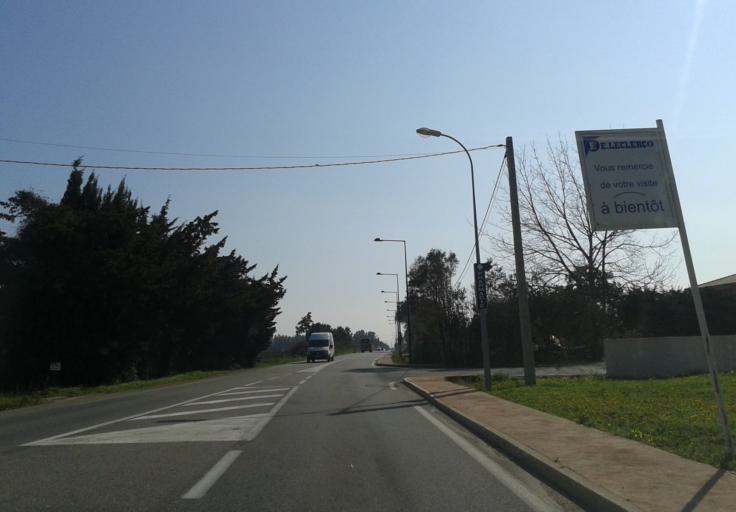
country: FR
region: Corsica
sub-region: Departement de la Haute-Corse
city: Linguizzetta
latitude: 42.2619
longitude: 9.5479
